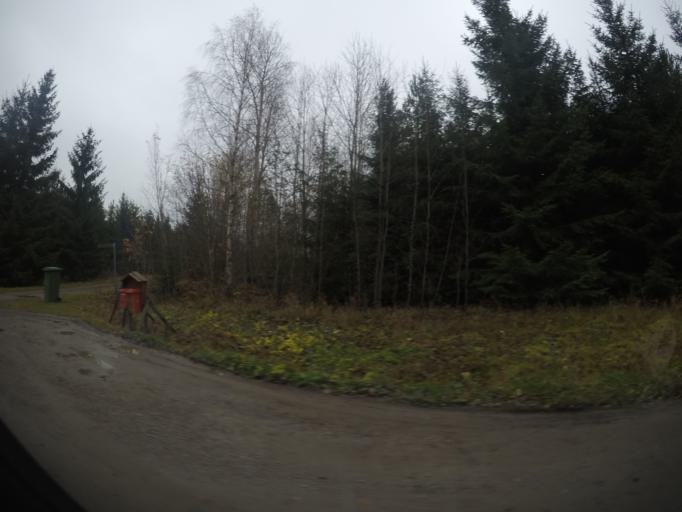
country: SE
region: Vaestmanland
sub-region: Surahammars Kommun
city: Ramnas
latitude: 59.7305
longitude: 16.1073
